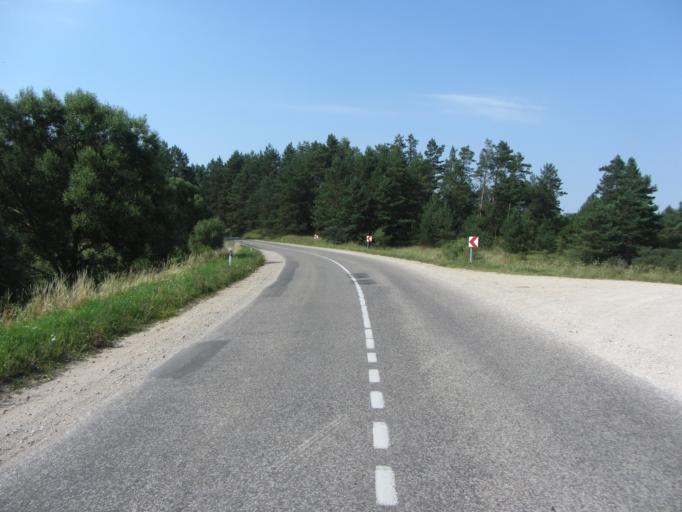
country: LT
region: Alytaus apskritis
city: Druskininkai
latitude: 54.1806
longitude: 23.8748
